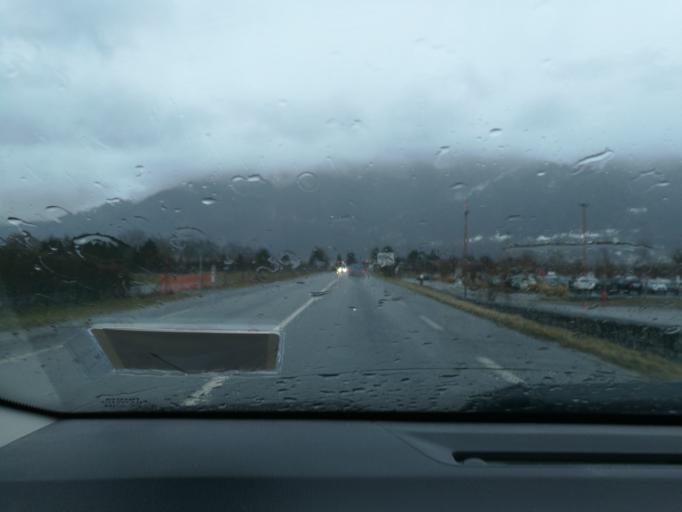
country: FR
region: Rhone-Alpes
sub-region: Departement de la Haute-Savoie
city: Passy
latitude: 45.9171
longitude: 6.6912
